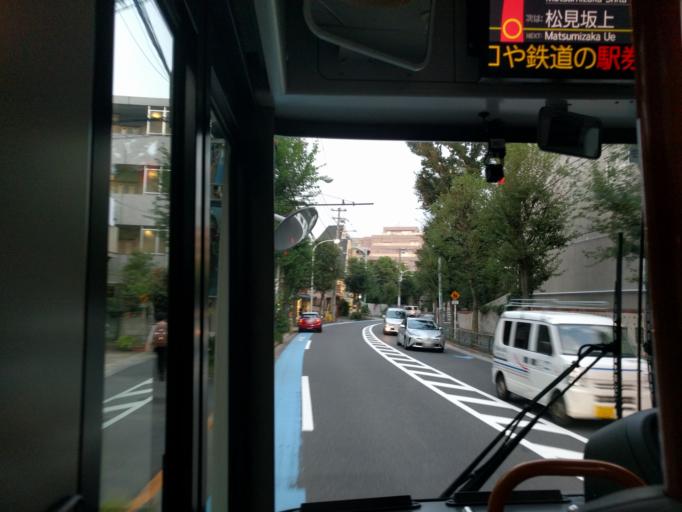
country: JP
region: Tokyo
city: Tokyo
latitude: 35.6559
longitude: 139.6842
